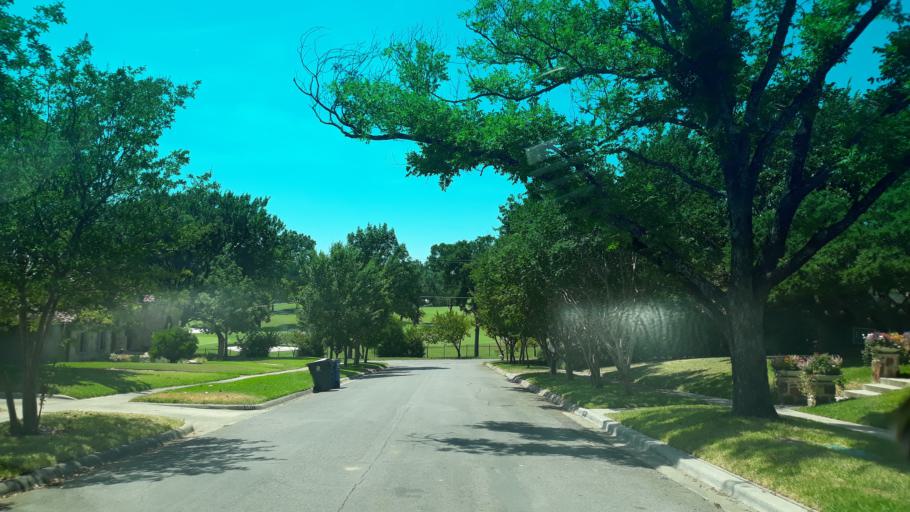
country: US
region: Texas
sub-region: Dallas County
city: Highland Park
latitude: 32.8127
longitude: -96.7430
